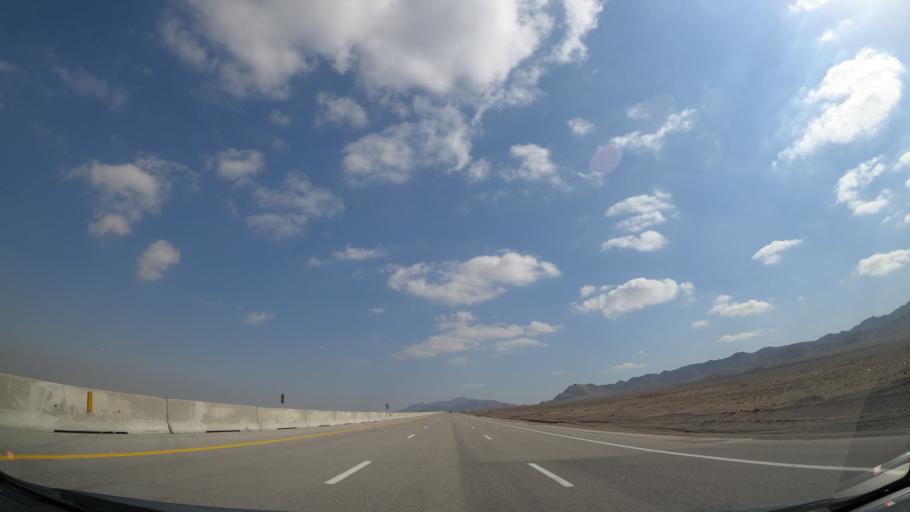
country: IR
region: Alborz
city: Eshtehard
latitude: 35.7134
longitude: 50.5875
